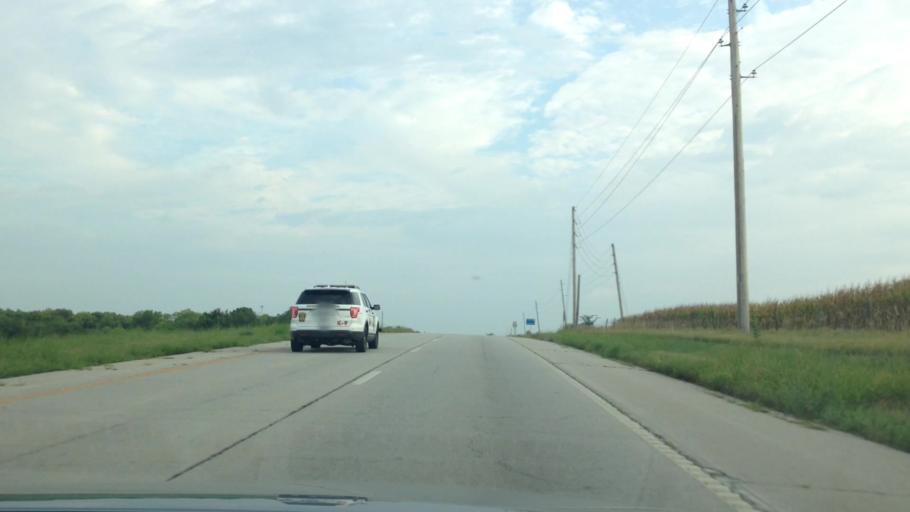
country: US
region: Missouri
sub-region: Clay County
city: Smithville
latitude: 39.3266
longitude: -94.5845
